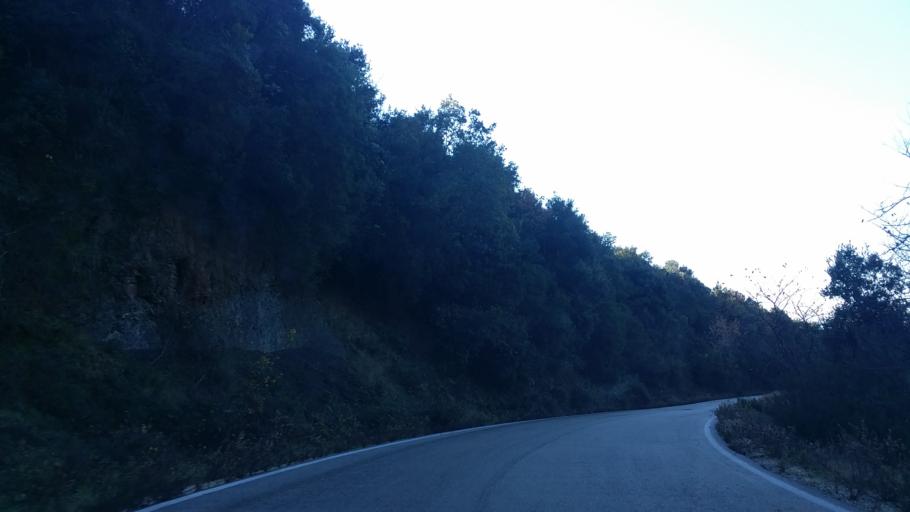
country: GR
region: West Greece
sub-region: Nomos Aitolias kai Akarnanias
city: Krikellos
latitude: 38.9647
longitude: 21.2344
